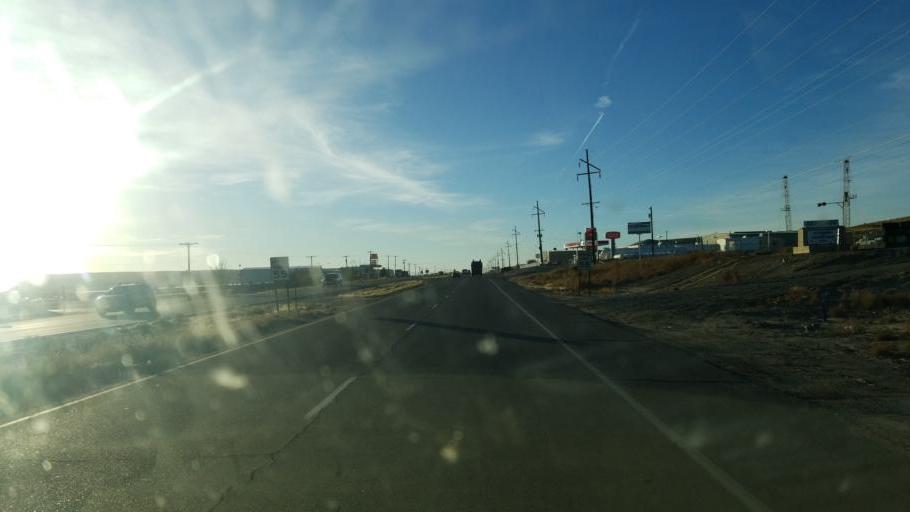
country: US
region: New Mexico
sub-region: San Juan County
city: Lee Acres
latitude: 36.7036
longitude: -108.1020
